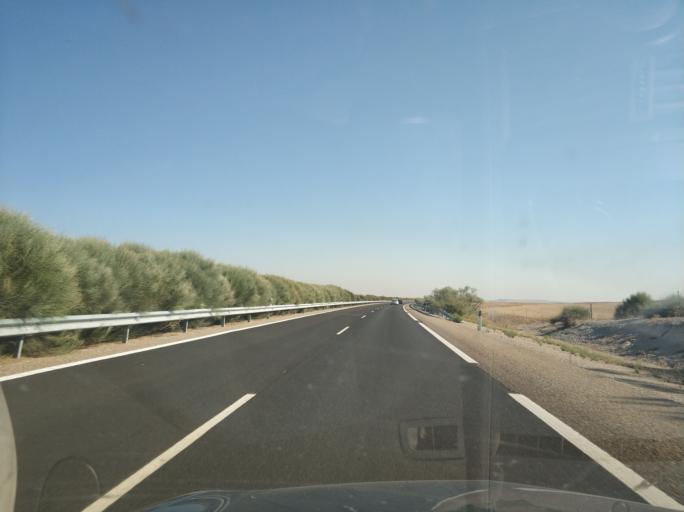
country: ES
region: Castille and Leon
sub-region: Provincia de Valladolid
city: Alaejos
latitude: 41.2748
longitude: -5.2557
